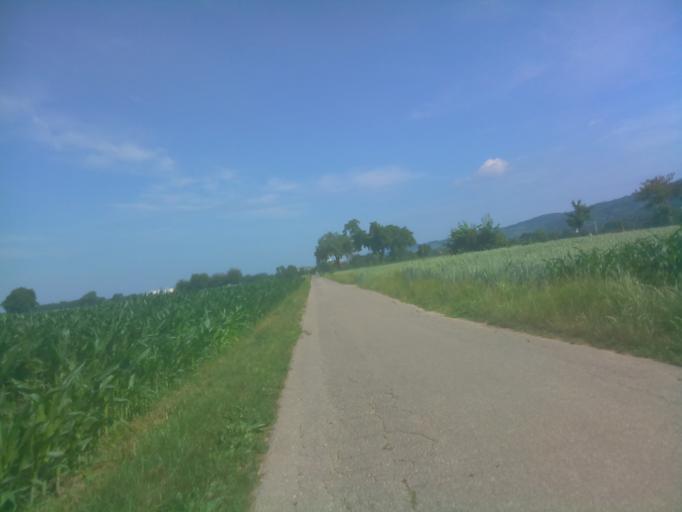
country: DE
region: Baden-Wuerttemberg
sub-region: Karlsruhe Region
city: Hemsbach
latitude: 49.5689
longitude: 8.6487
